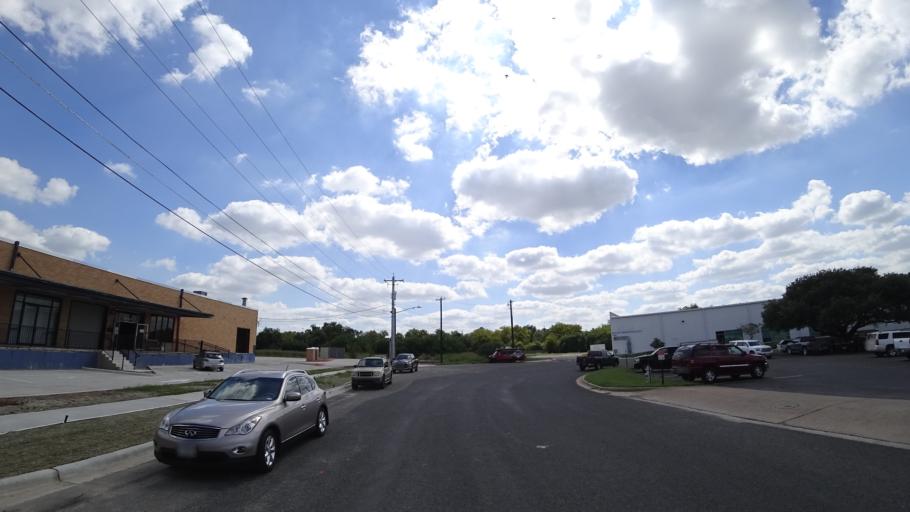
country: US
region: Texas
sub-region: Travis County
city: Austin
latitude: 30.3261
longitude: -97.7174
